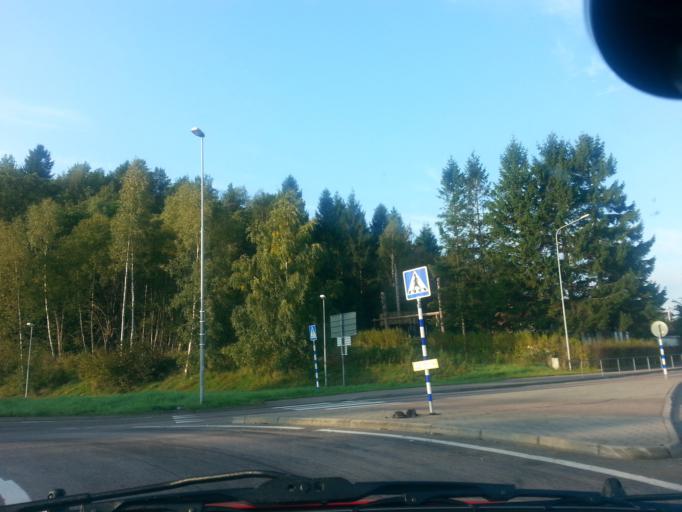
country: SE
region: Vaestra Goetaland
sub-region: Partille Kommun
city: Furulund
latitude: 57.7391
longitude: 12.1319
